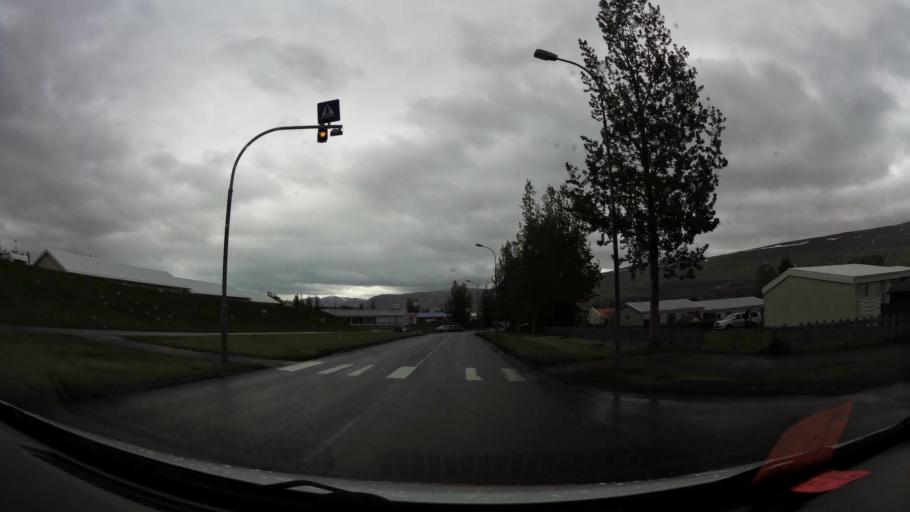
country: IS
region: Northeast
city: Akureyri
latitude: 65.6935
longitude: -18.1278
